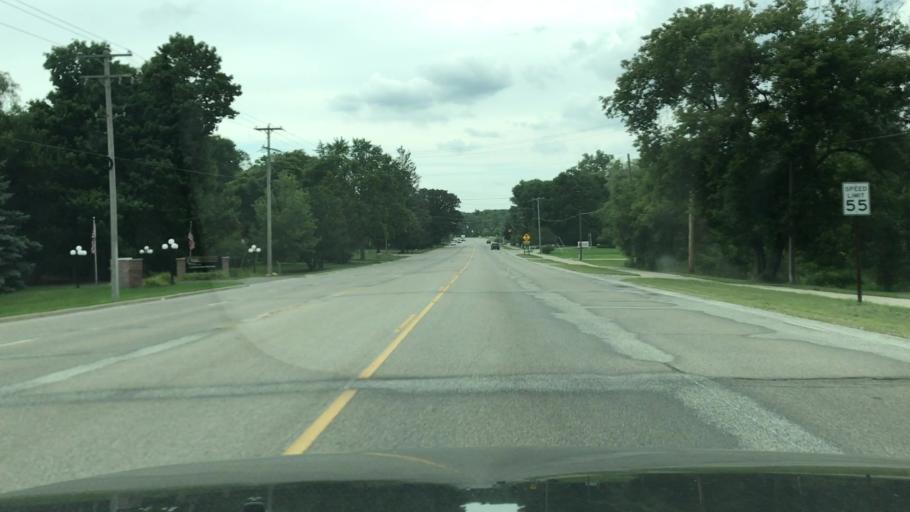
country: US
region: Michigan
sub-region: Kent County
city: Forest Hills
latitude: 42.9175
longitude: -85.5026
